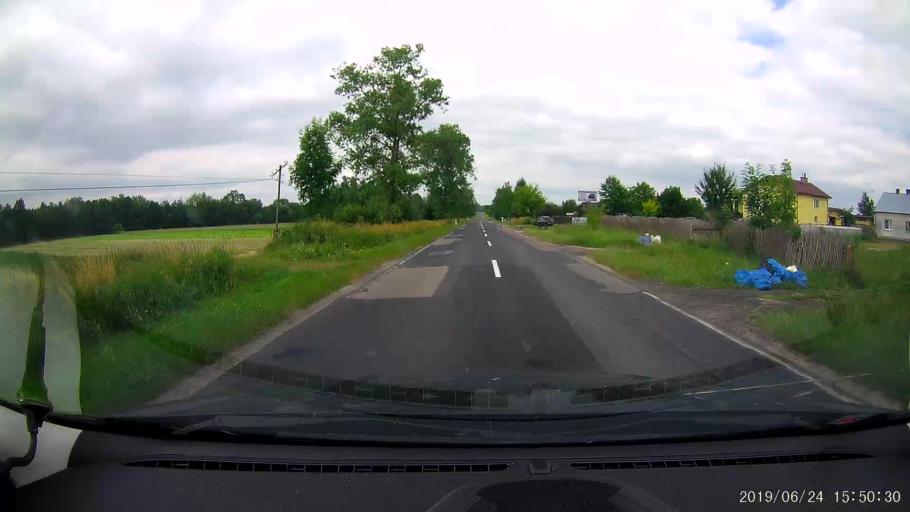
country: PL
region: Subcarpathian Voivodeship
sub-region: Powiat lubaczowski
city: Oleszyce
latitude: 50.1780
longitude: 23.0593
